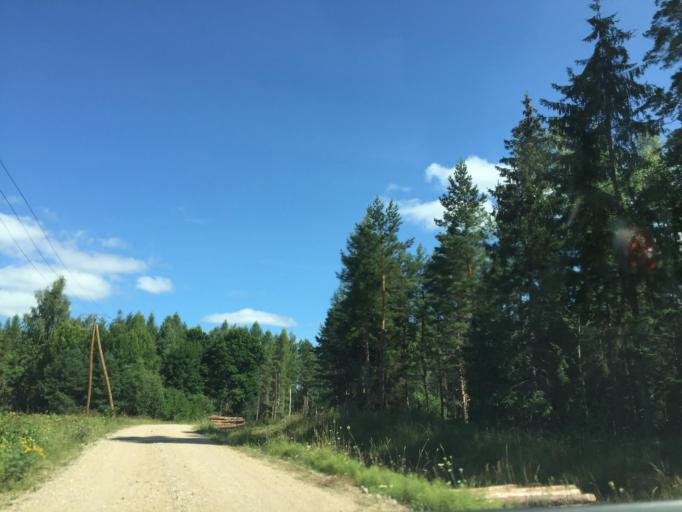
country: LV
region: Talsu Rajons
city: Stende
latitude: 57.1686
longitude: 22.2994
